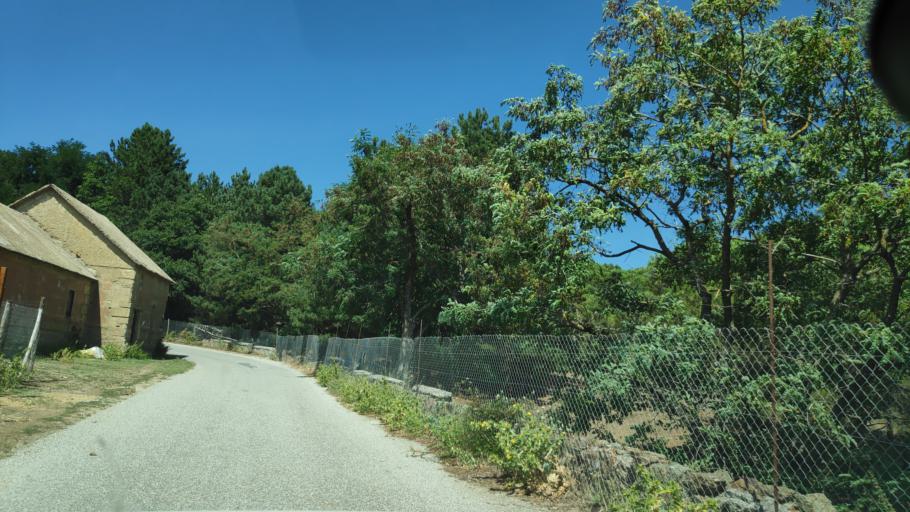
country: IT
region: Calabria
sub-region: Provincia di Reggio Calabria
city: Bova
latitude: 38.0169
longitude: 15.9349
